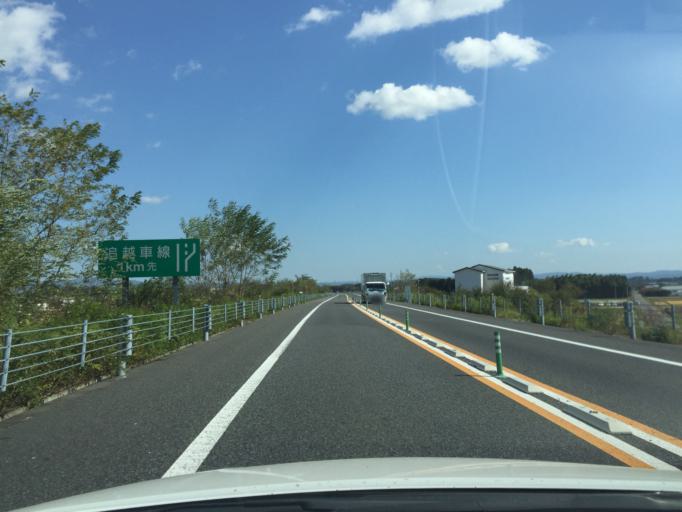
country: JP
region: Fukushima
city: Sukagawa
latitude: 37.1879
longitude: 140.3200
